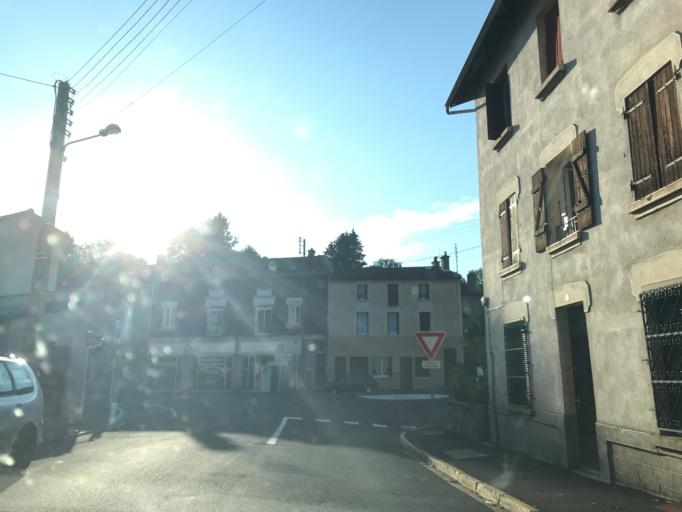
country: FR
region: Auvergne
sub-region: Departement du Puy-de-Dome
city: La Monnerie-le-Montel
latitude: 45.8703
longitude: 3.6078
